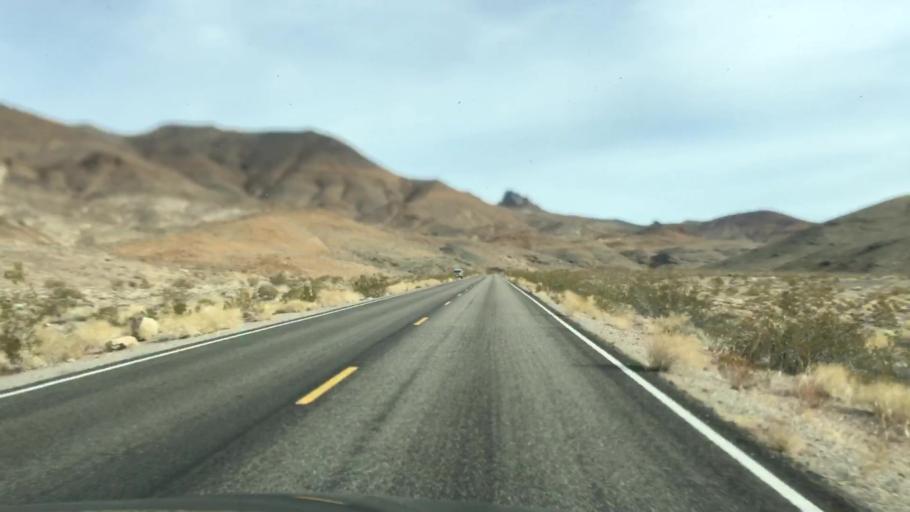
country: US
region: Nevada
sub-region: Nye County
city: Beatty
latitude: 36.7377
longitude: -116.9692
